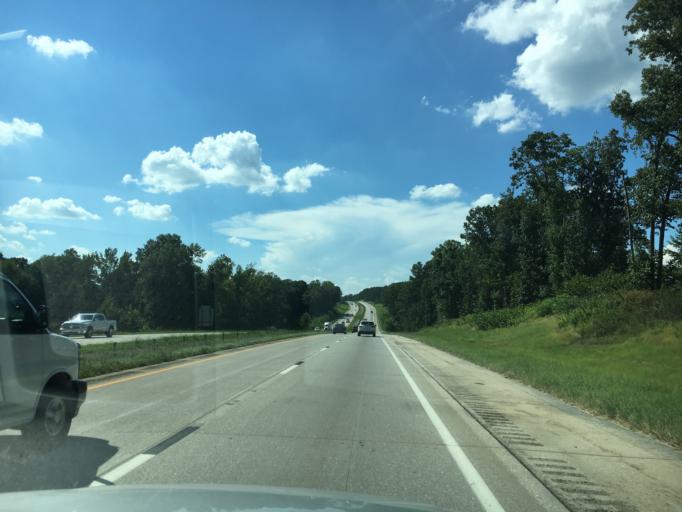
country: US
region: South Carolina
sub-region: Laurens County
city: Clinton
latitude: 34.5223
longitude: -81.9127
